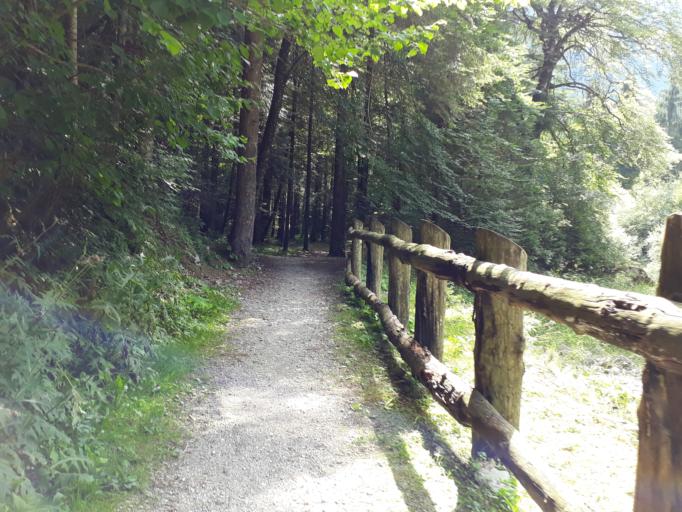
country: IT
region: Trentino-Alto Adige
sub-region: Provincia di Trento
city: Pieve di Ledro
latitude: 45.9369
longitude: 10.7383
